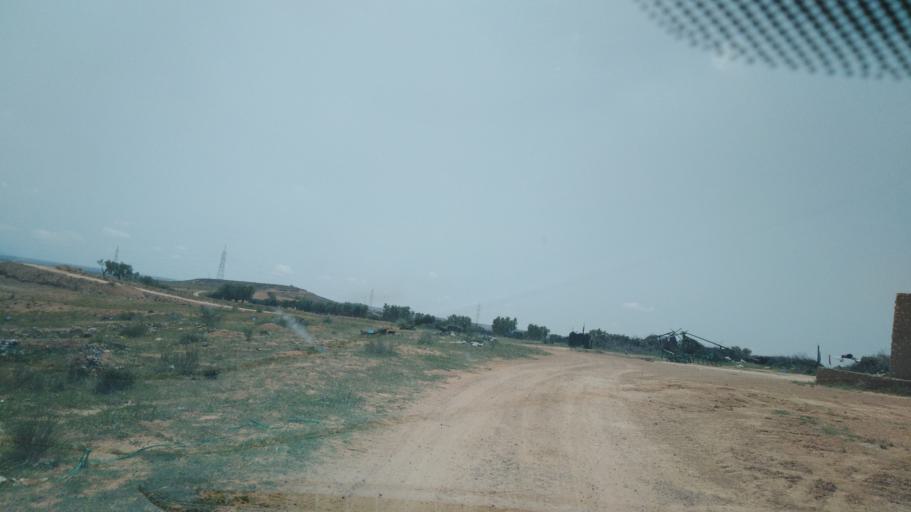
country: TN
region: Safaqis
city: Sfax
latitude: 34.7679
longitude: 10.5786
